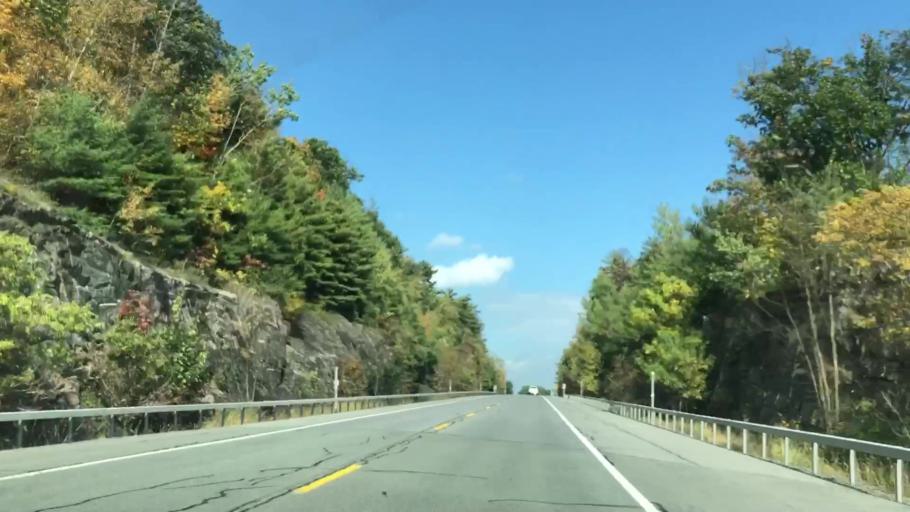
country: US
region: New York
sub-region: Washington County
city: Whitehall
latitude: 43.4533
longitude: -73.4478
